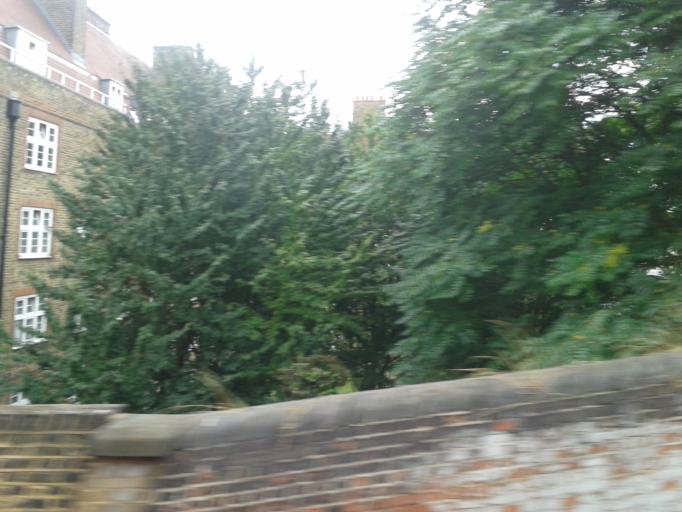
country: GB
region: England
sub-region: Greater London
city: Bethnal Green
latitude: 51.5119
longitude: -0.0533
